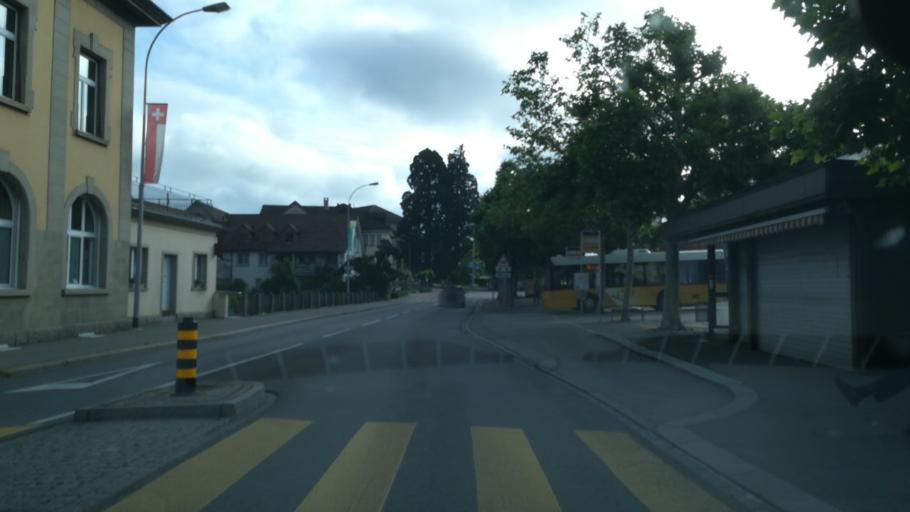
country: CH
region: Saint Gallen
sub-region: Wahlkreis Wil
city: Niederburen
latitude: 47.4924
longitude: 9.2417
